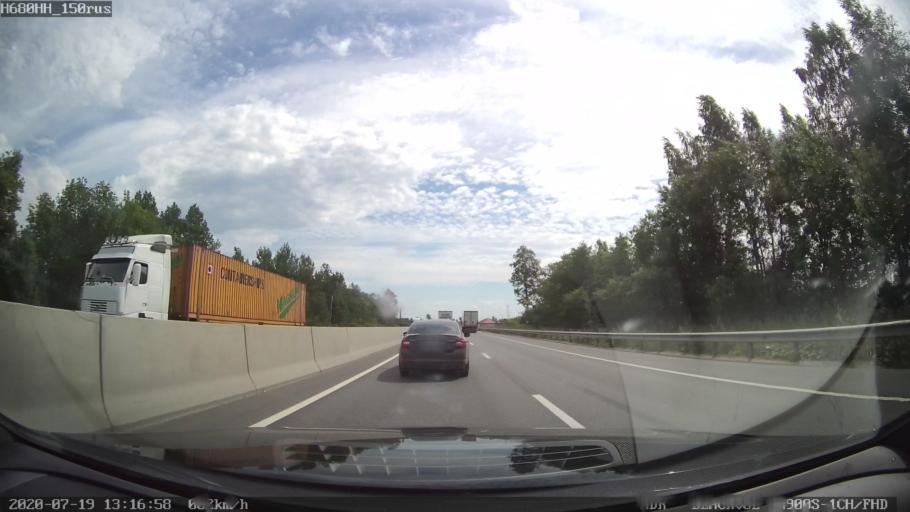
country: RU
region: St.-Petersburg
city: Kolpino
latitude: 59.7128
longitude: 30.5627
